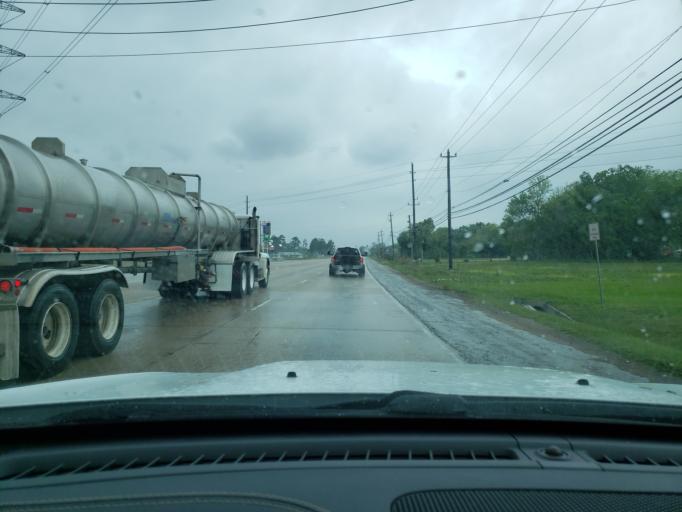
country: US
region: Texas
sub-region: Chambers County
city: Mont Belvieu
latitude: 29.7978
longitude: -94.9062
